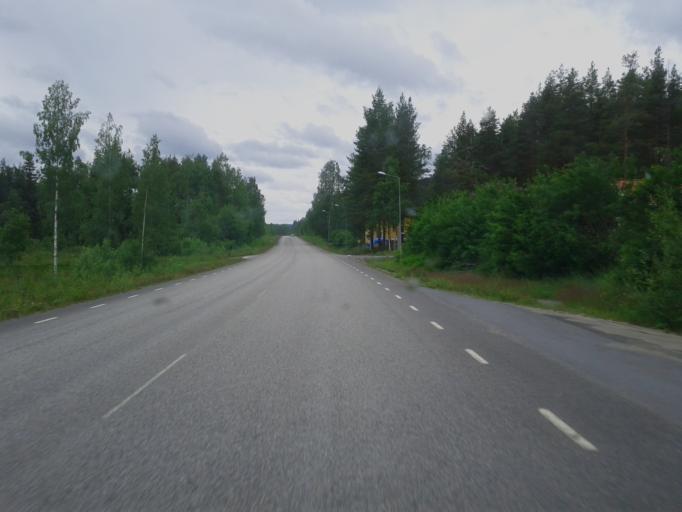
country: SE
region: Vaesterbotten
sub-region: Skelleftea Kommun
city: Langsele
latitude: 64.9171
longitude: 20.0966
